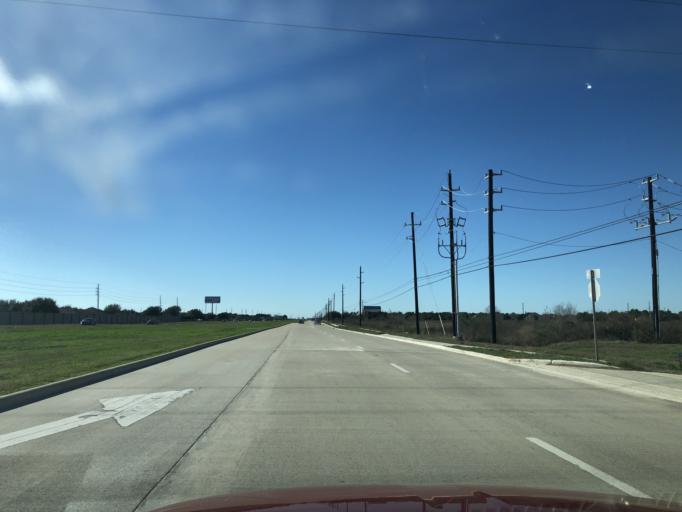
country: US
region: Texas
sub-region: Fort Bend County
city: Cinco Ranch
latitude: 29.6970
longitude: -95.8223
